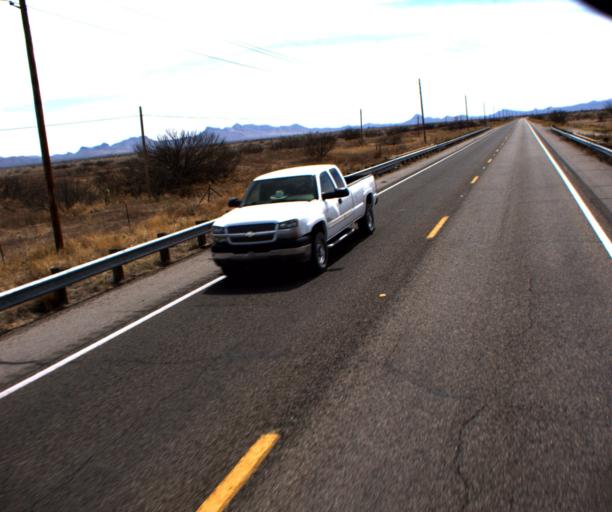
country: US
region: Arizona
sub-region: Cochise County
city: Pirtleville
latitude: 31.4418
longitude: -109.5963
